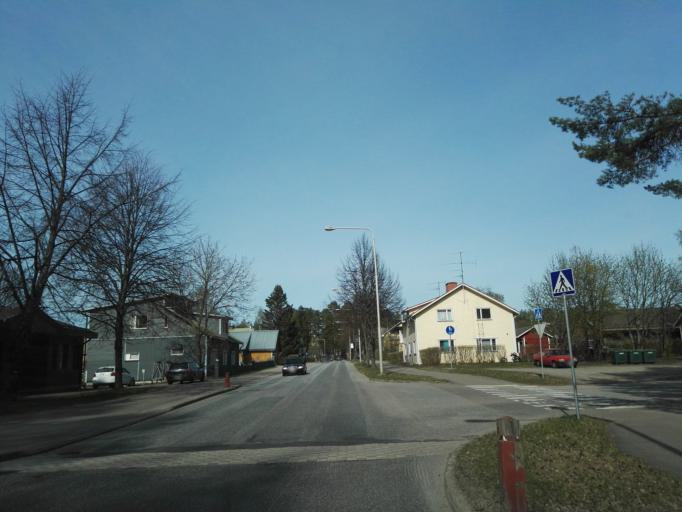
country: FI
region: Central Finland
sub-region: Joutsa
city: Joutsa
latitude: 61.7434
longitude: 26.1173
